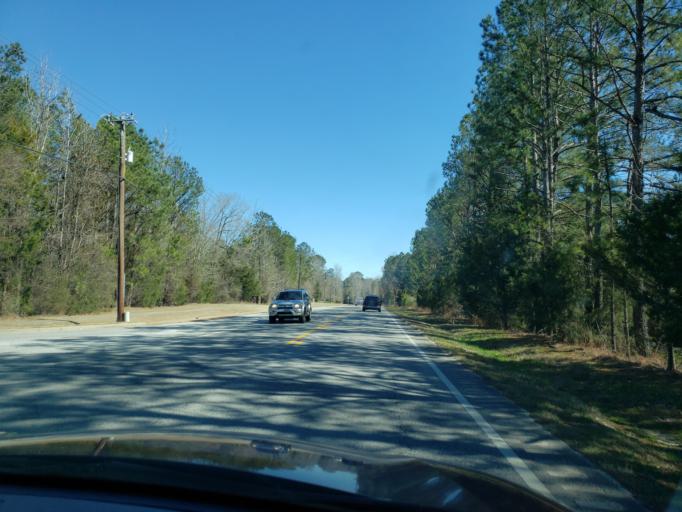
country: US
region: Alabama
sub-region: Lee County
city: Auburn
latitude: 32.5986
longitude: -85.5639
